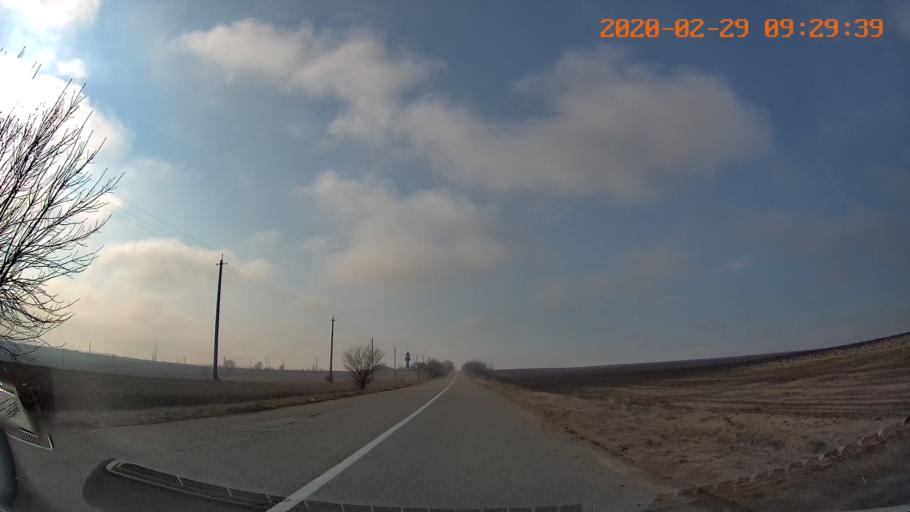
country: UA
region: Odessa
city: Lymanske
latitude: 46.6760
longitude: 29.9202
